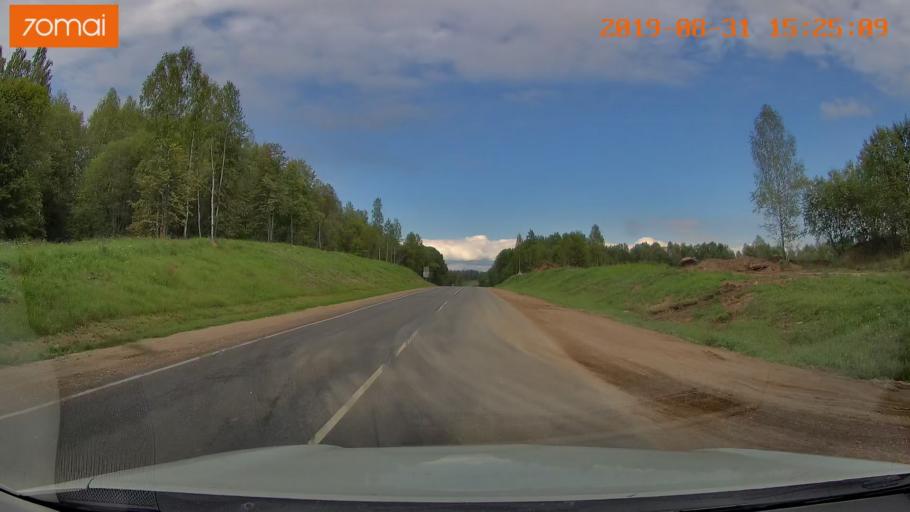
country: RU
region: Kaluga
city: Baryatino
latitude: 54.5374
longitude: 34.5153
